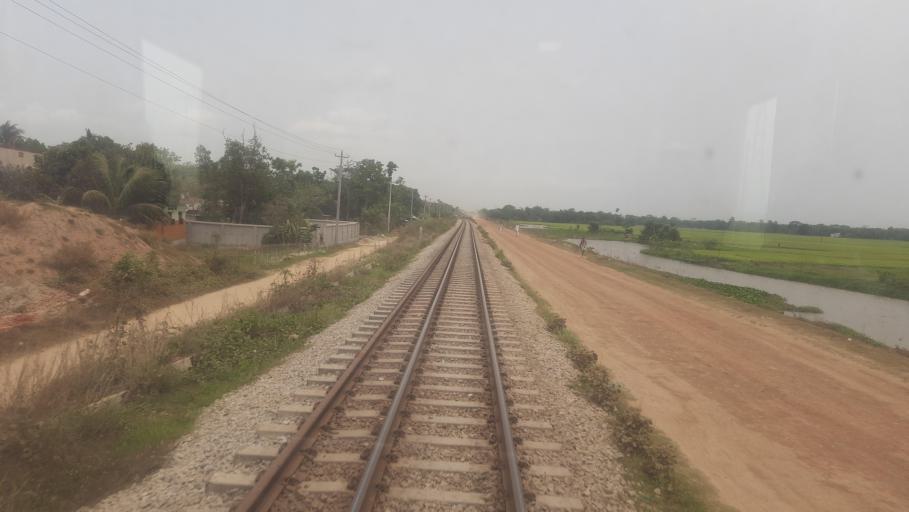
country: BD
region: Chittagong
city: Comilla
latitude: 23.5048
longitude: 91.1659
